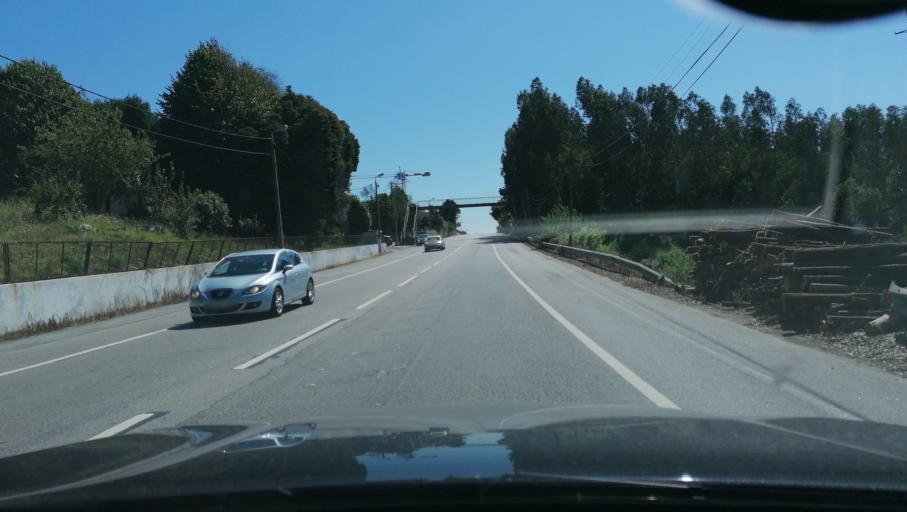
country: PT
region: Porto
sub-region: Vila Nova de Gaia
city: Gulpilhares
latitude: 41.0815
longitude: -8.6357
